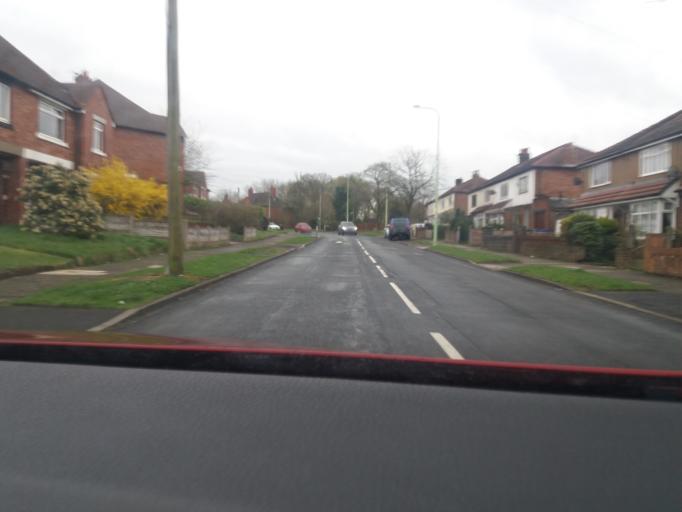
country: GB
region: England
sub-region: Lancashire
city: Coppull
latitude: 53.6402
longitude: -2.6437
